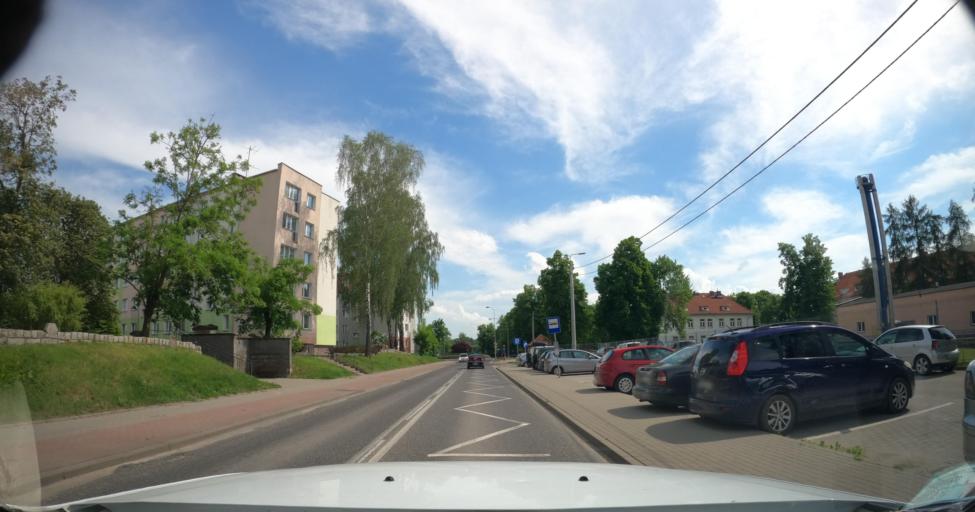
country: PL
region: Warmian-Masurian Voivodeship
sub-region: Powiat lidzbarski
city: Lidzbark Warminski
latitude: 54.1281
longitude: 20.5659
